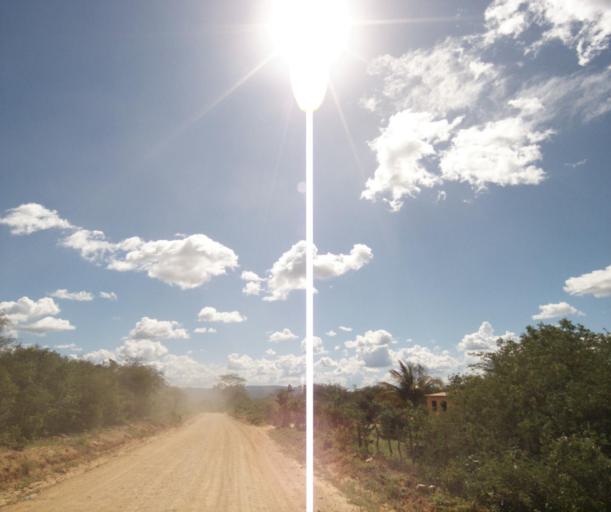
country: BR
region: Bahia
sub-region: Pocoes
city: Pocoes
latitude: -14.2521
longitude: -40.7101
